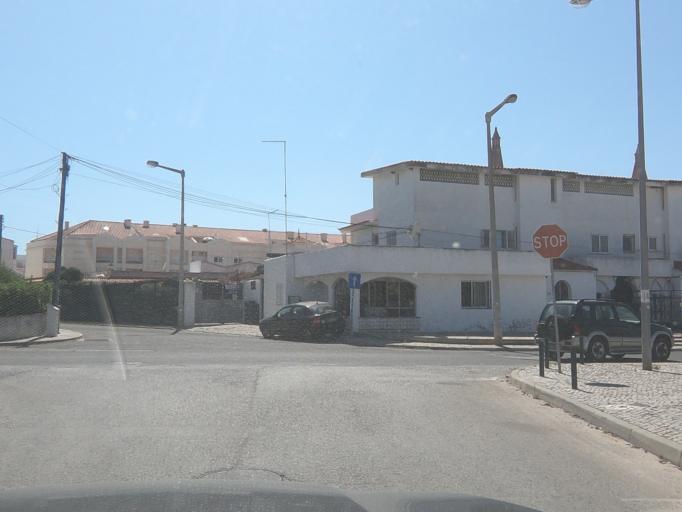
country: PT
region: Faro
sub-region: Loule
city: Quarteira
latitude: 37.0755
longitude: -8.0977
